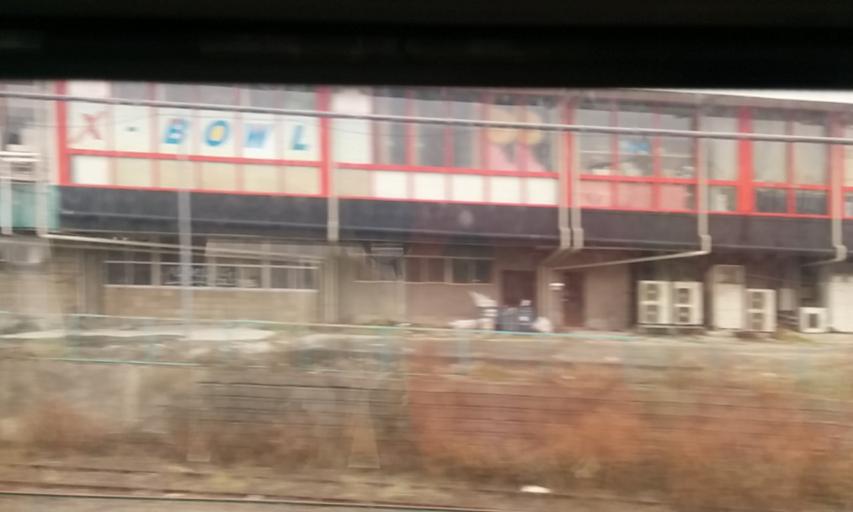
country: JP
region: Nagano
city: Matsumoto
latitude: 36.2017
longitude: 137.9664
